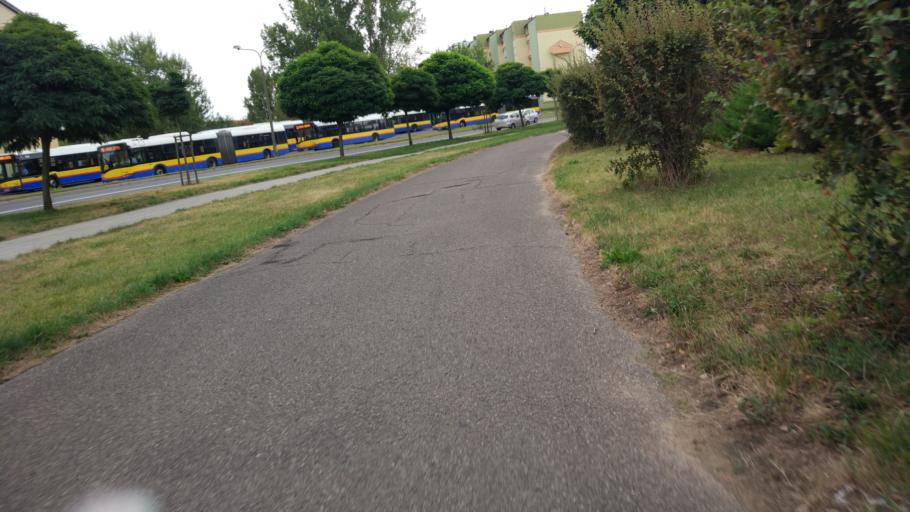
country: PL
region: Masovian Voivodeship
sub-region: Plock
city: Plock
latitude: 52.5310
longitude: 19.7594
